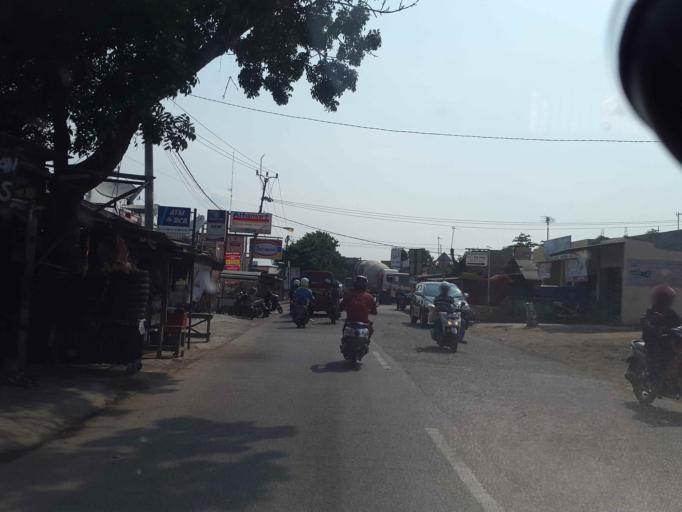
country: ID
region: West Java
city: Cikarang
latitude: -6.2171
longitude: 107.1659
